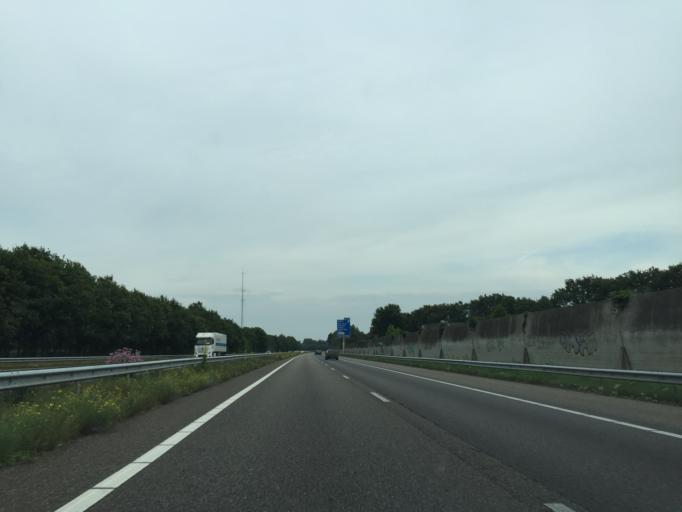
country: NL
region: North Brabant
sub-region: Gemeente Bernheze
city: Heesch
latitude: 51.7379
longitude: 5.5442
